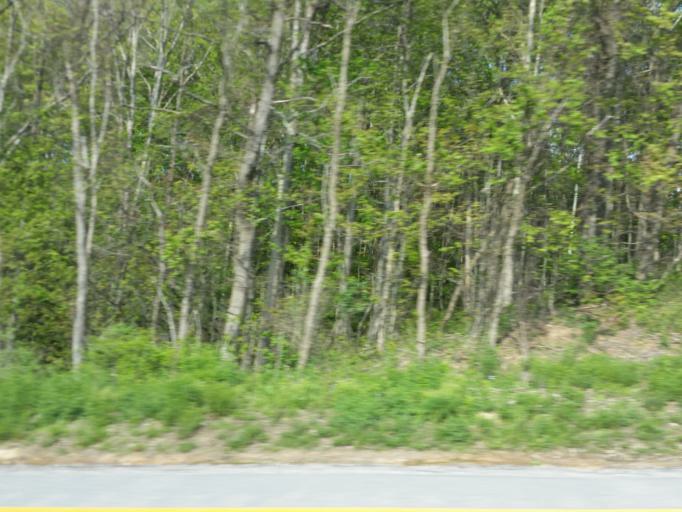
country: US
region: West Virginia
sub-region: Raleigh County
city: Shady Spring
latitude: 37.6516
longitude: -81.1130
